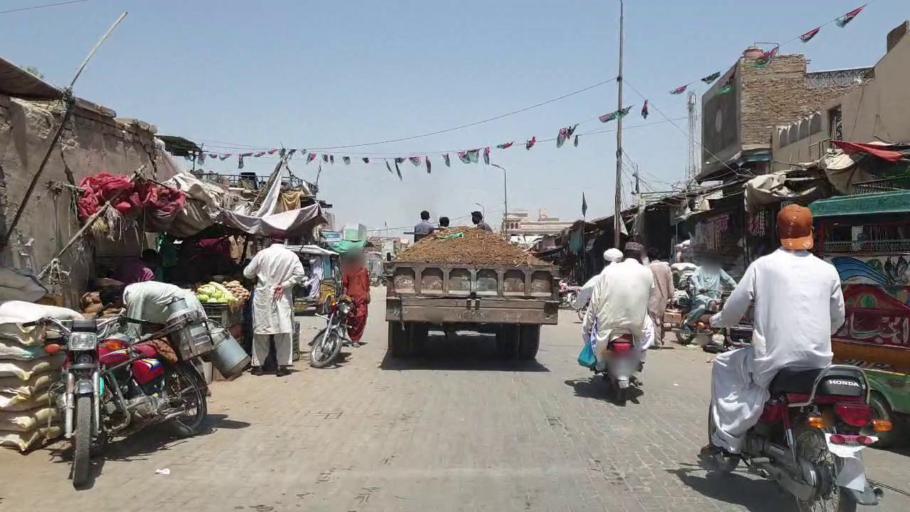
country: PK
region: Sindh
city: Adilpur
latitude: 27.9377
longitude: 69.3203
